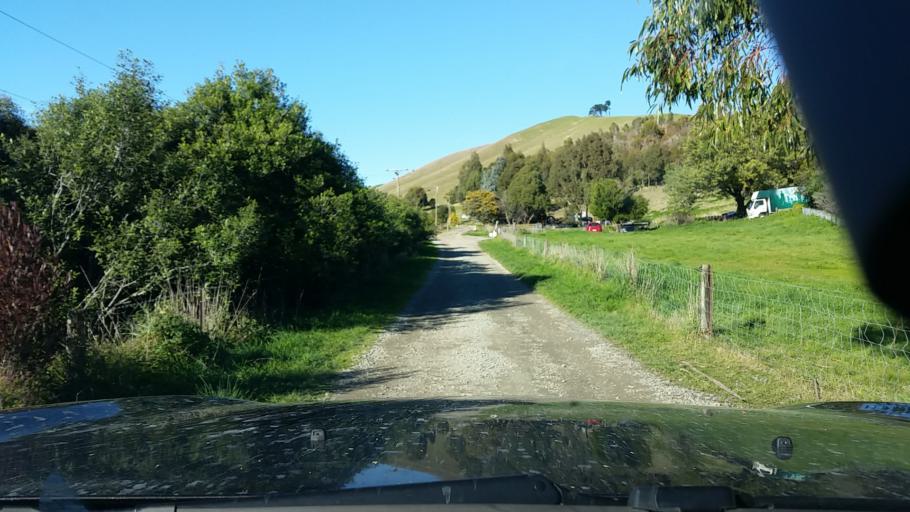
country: NZ
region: Marlborough
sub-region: Marlborough District
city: Blenheim
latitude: -41.5435
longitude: 173.9627
